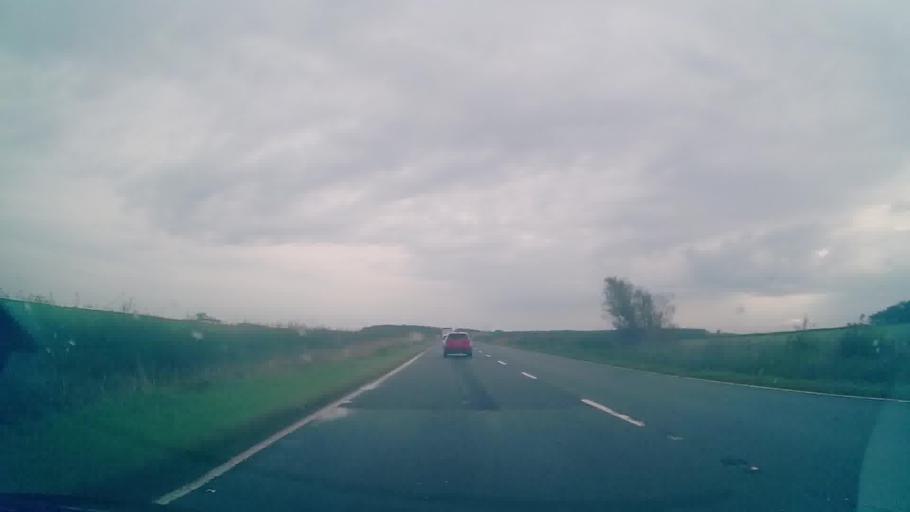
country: GB
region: Scotland
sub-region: Dumfries and Galloway
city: Annan
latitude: 55.0048
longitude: -3.3215
